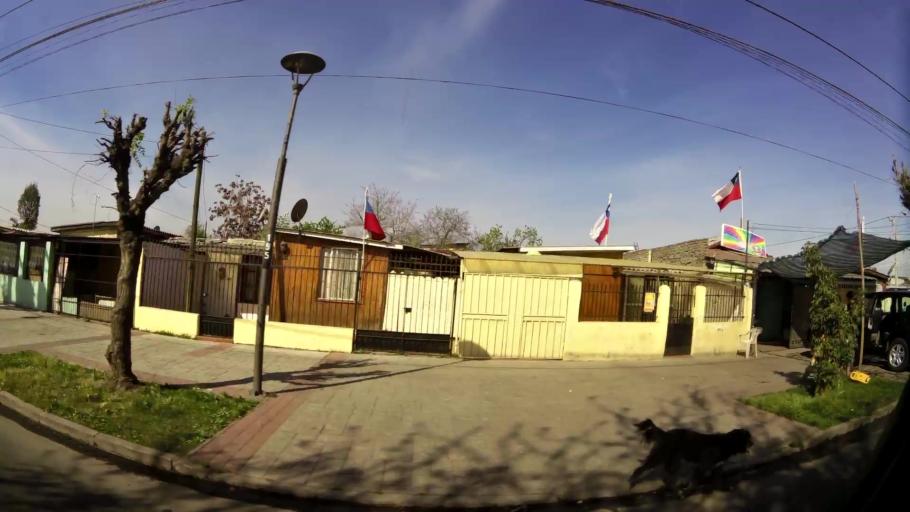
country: CL
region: Santiago Metropolitan
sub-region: Provincia de Santiago
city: La Pintana
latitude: -33.5353
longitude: -70.6292
